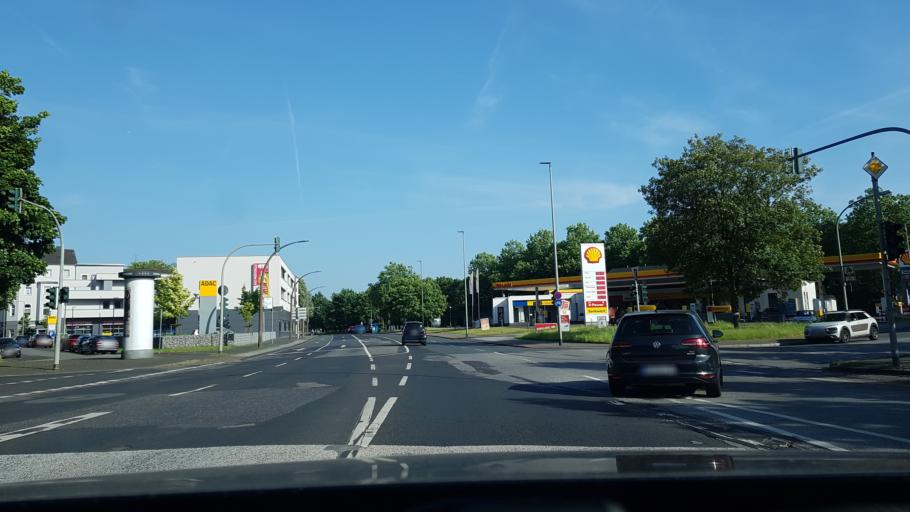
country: DE
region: North Rhine-Westphalia
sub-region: Regierungsbezirk Dusseldorf
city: Duisburg
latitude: 51.4285
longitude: 6.7587
